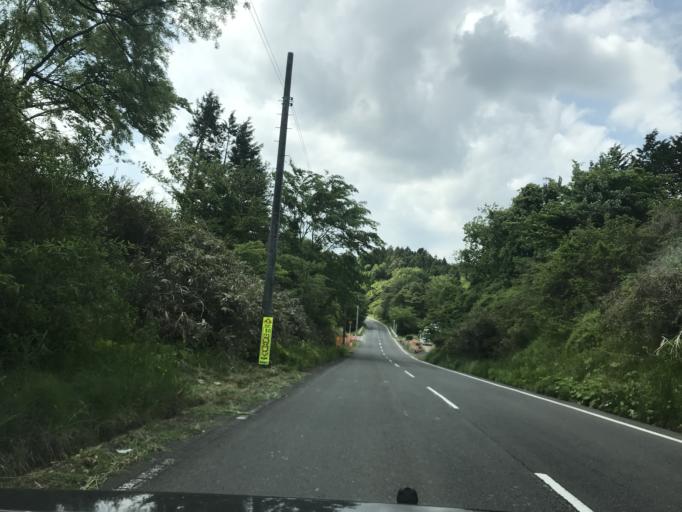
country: JP
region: Miyagi
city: Furukawa
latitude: 38.7616
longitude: 140.9398
